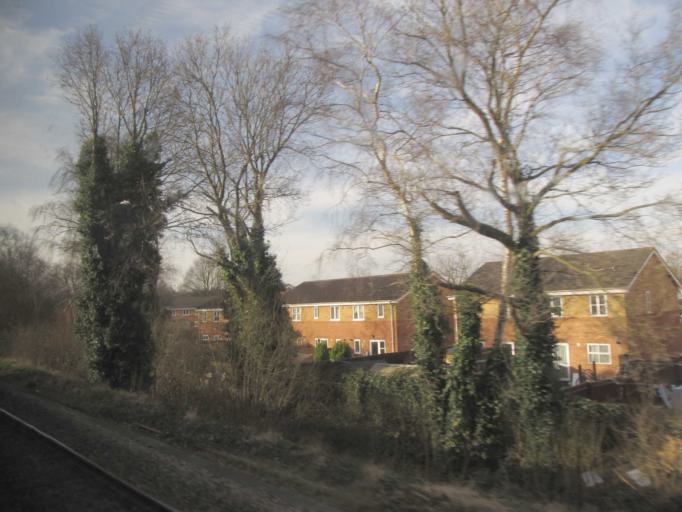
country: GB
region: England
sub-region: Surrey
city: Seale
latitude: 51.2613
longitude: -0.7248
